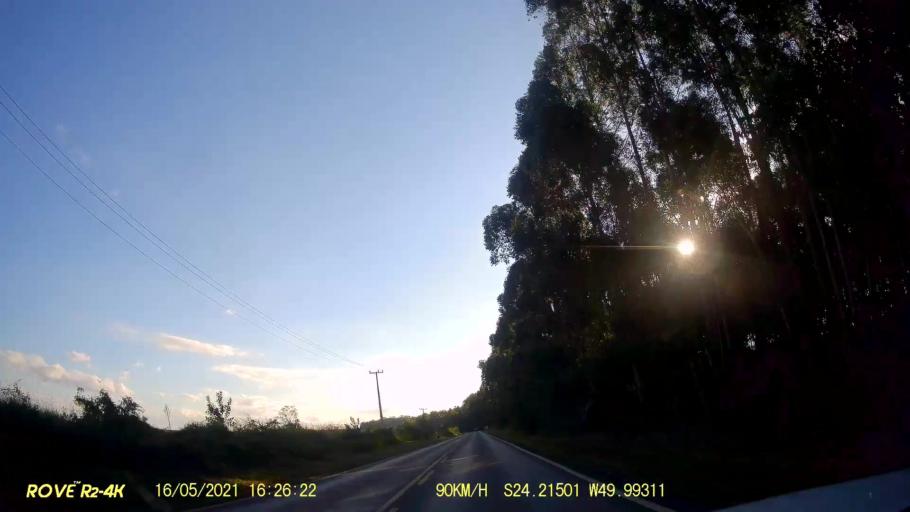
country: BR
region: Parana
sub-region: Jaguariaiva
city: Jaguariaiva
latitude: -24.2150
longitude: -49.9932
